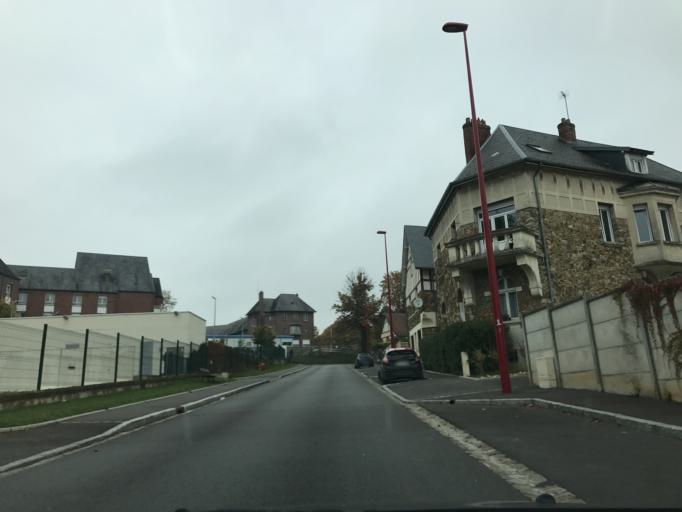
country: FR
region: Picardie
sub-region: Departement de la Somme
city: Peronne
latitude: 49.9331
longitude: 2.9306
